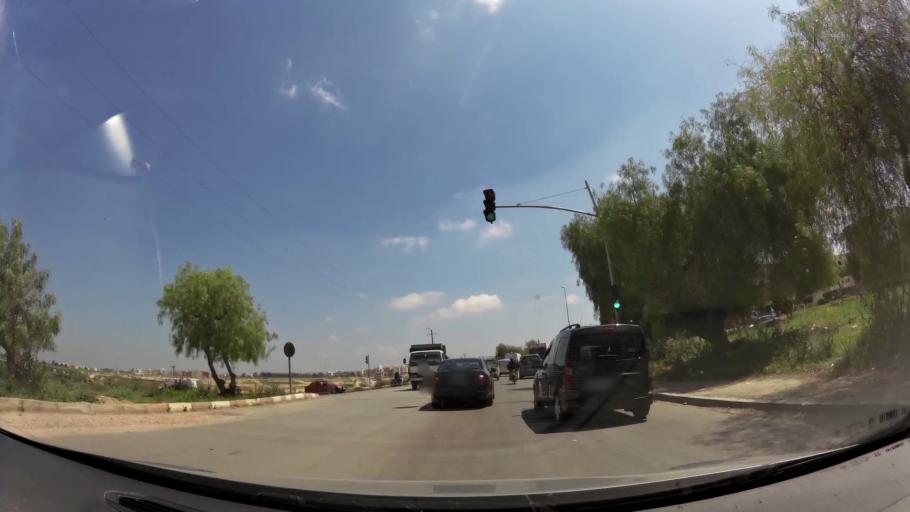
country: MA
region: Fes-Boulemane
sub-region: Fes
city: Fes
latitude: 34.0016
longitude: -5.0434
